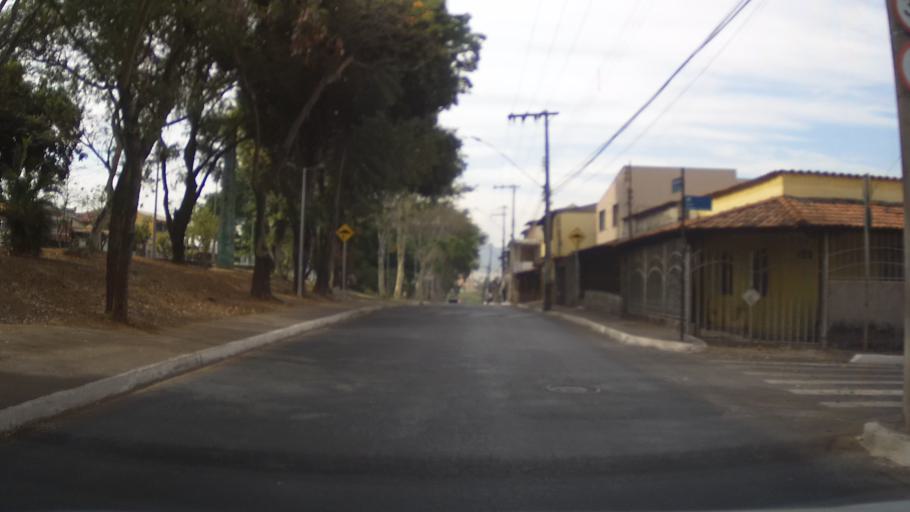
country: BR
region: Minas Gerais
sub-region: Contagem
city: Contagem
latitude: -19.9336
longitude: -44.0292
